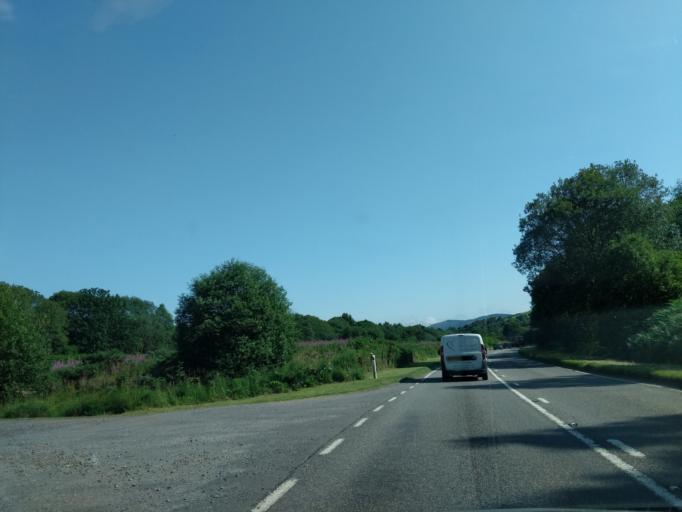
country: GB
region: Scotland
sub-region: Moray
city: Rothes
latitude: 57.5140
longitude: -3.2060
